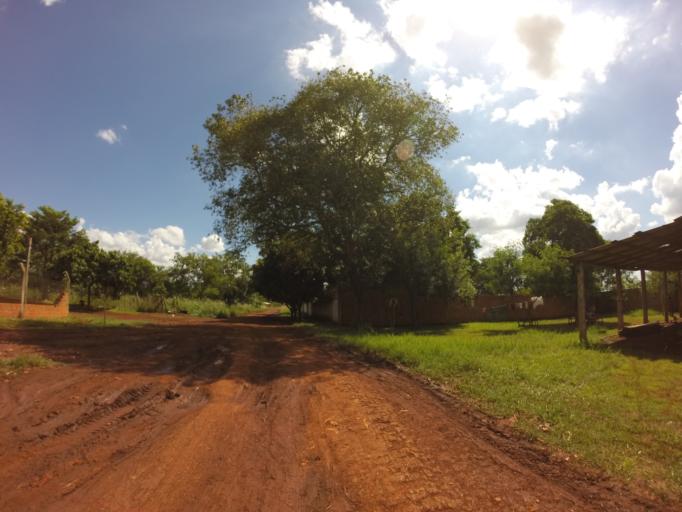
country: PY
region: Alto Parana
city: Ciudad del Este
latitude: -25.3711
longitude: -54.6507
